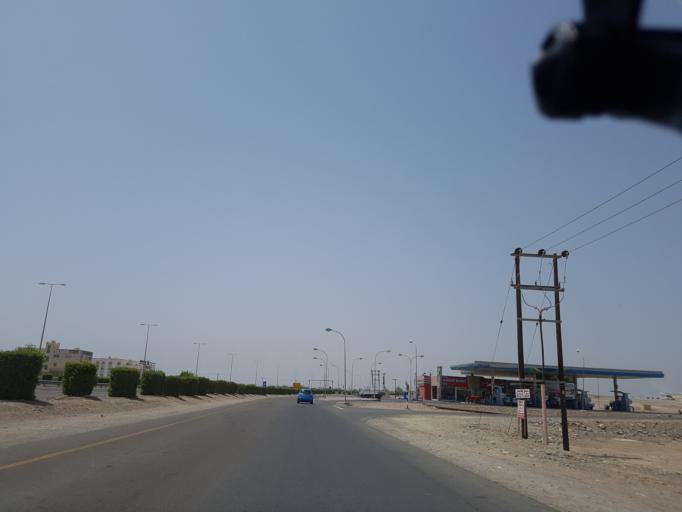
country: OM
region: Al Batinah
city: Al Liwa'
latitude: 24.4150
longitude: 56.6010
